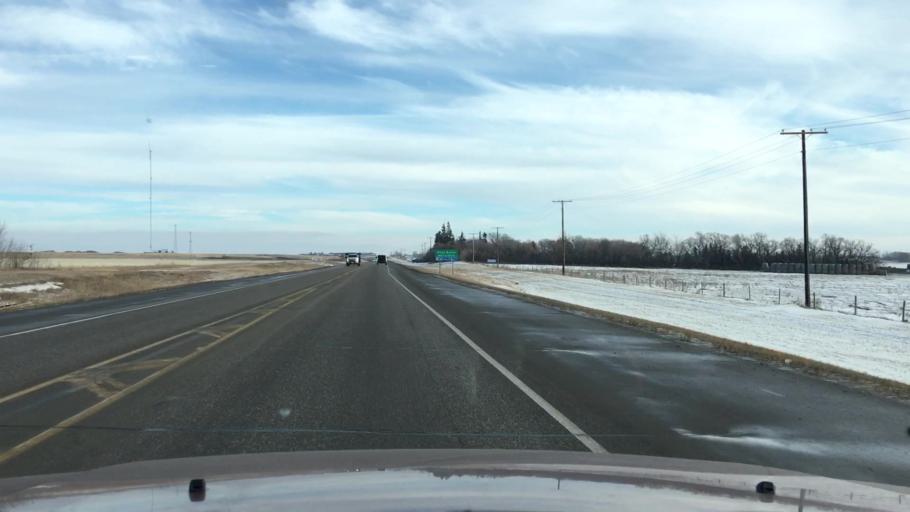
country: CA
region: Saskatchewan
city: Pilot Butte
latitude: 50.4844
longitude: -104.4537
